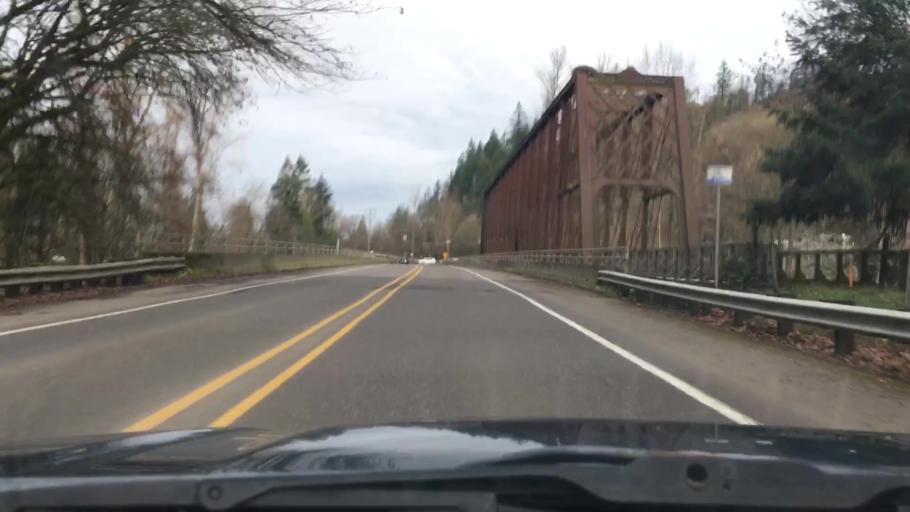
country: US
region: Oregon
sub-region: Lane County
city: Coburg
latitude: 44.1117
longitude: -123.0475
